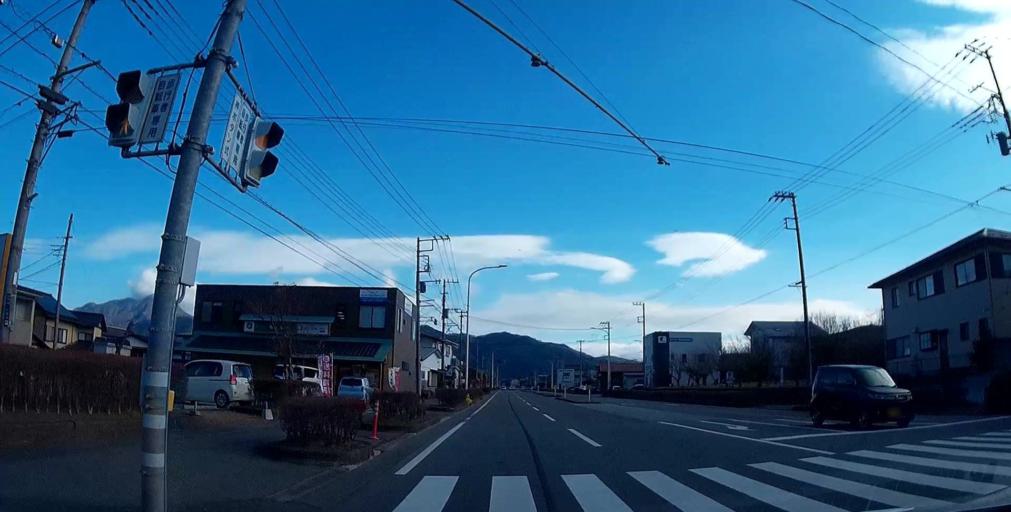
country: JP
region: Yamanashi
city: Fujikawaguchiko
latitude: 35.4888
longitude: 138.7965
